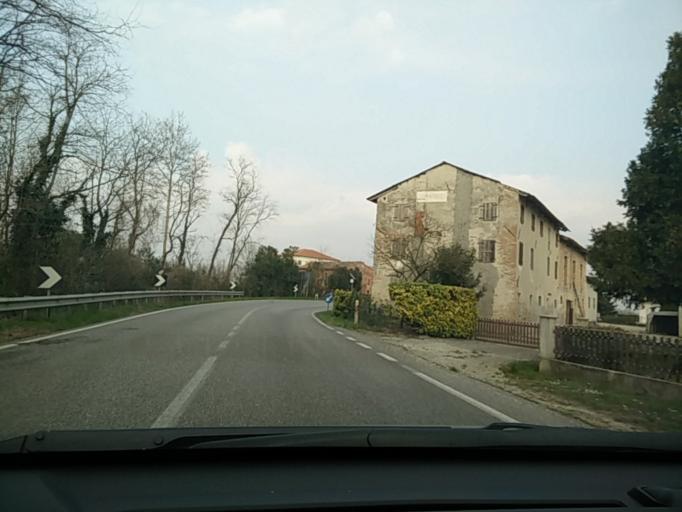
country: IT
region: Veneto
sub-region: Provincia di Treviso
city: Ormelle
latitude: 45.7842
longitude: 12.4440
